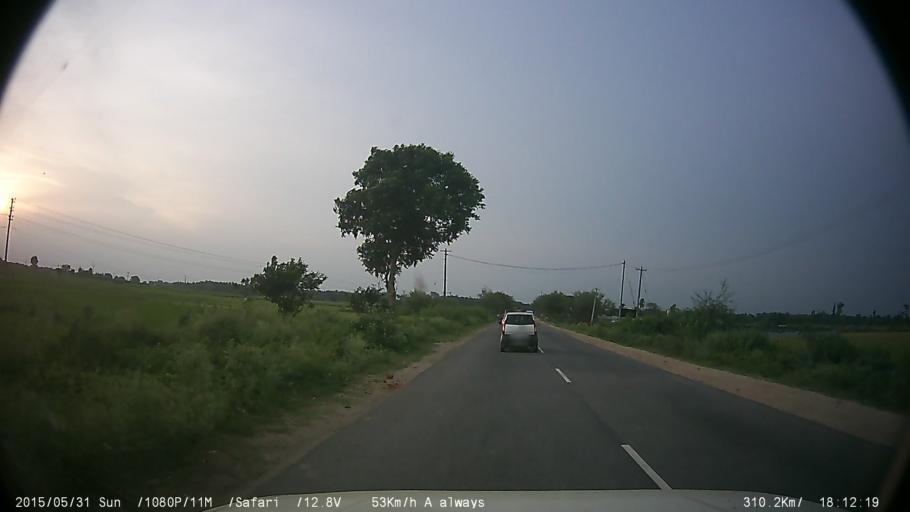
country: IN
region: Karnataka
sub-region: Mysore
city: Nanjangud
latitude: 12.0949
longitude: 76.6724
